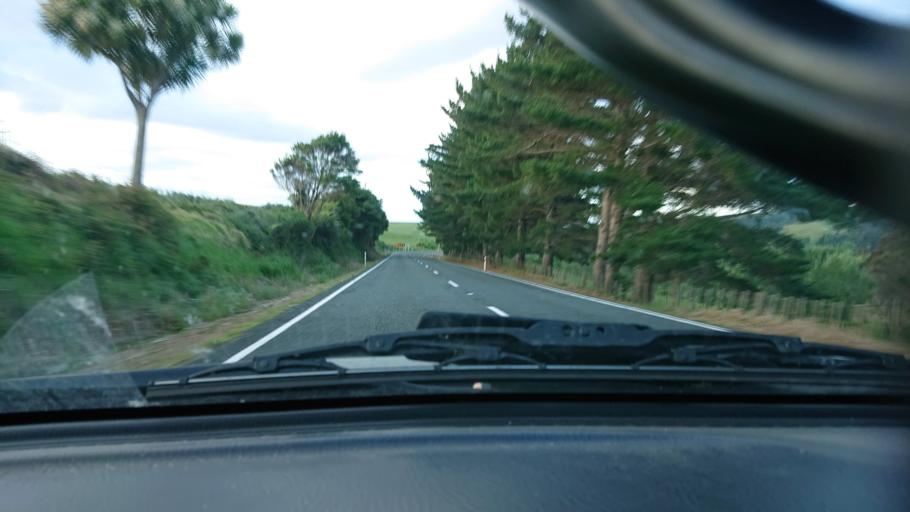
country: NZ
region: Auckland
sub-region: Auckland
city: Parakai
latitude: -36.4697
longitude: 174.4480
